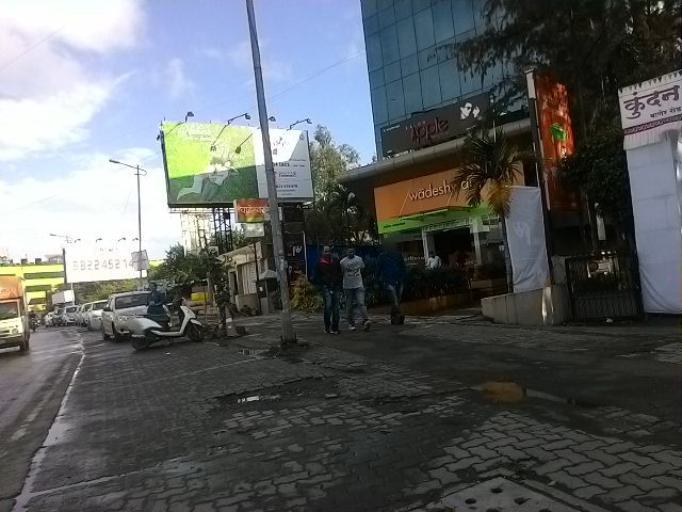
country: IN
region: Maharashtra
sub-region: Pune Division
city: Khadki
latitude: 18.5557
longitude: 73.7950
